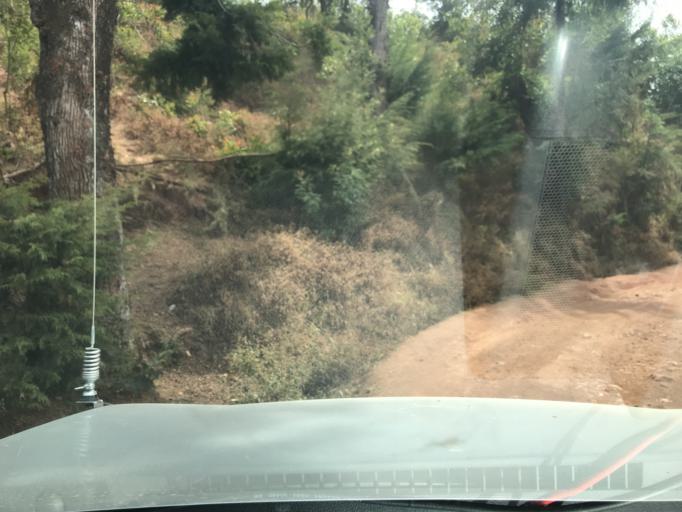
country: TL
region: Ainaro
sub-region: Ainaro
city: Ainaro
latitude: -8.8873
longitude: 125.5192
